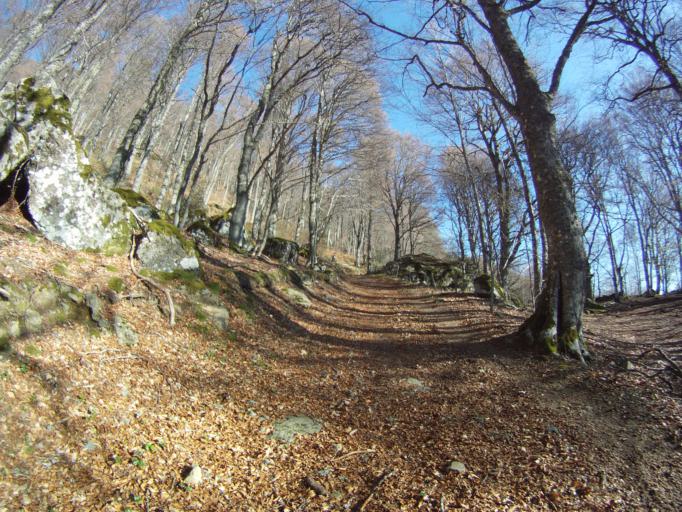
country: FR
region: Auvergne
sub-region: Departement du Puy-de-Dome
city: Mont-Dore
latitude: 45.5469
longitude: 2.8599
